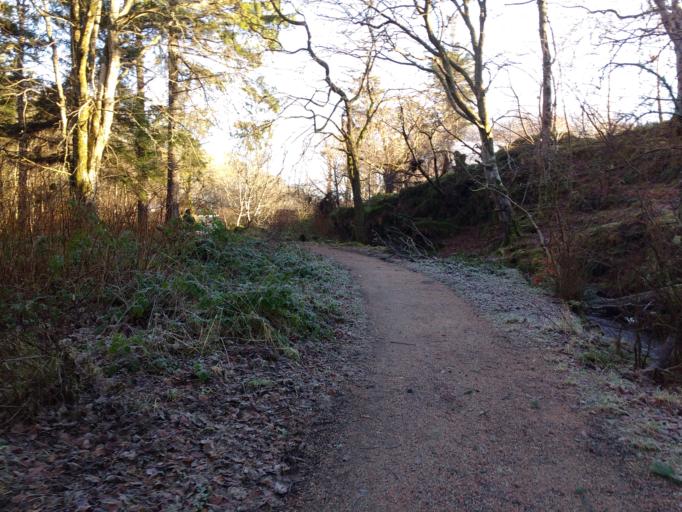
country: GB
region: Scotland
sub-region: Eilean Siar
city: Isle of Lewis
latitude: 58.2188
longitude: -6.3936
